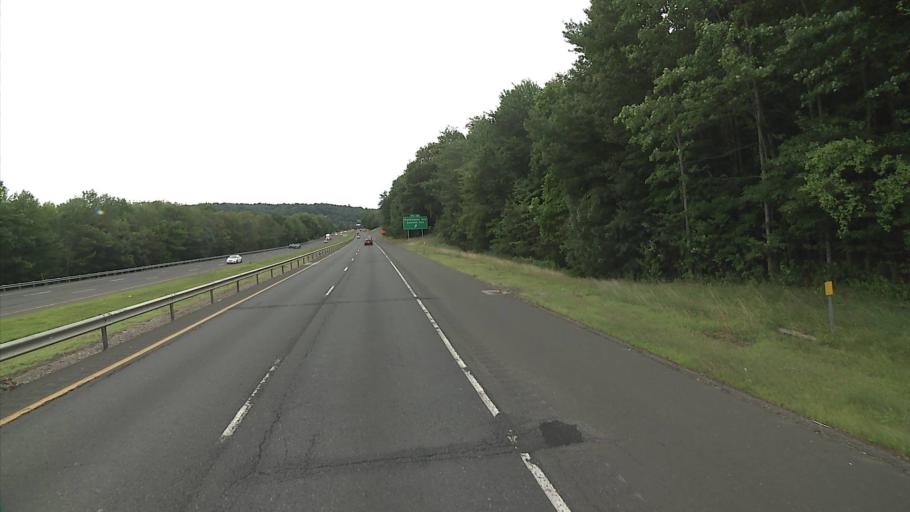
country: US
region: Connecticut
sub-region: Litchfield County
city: Oakville
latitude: 41.5909
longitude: -73.0605
